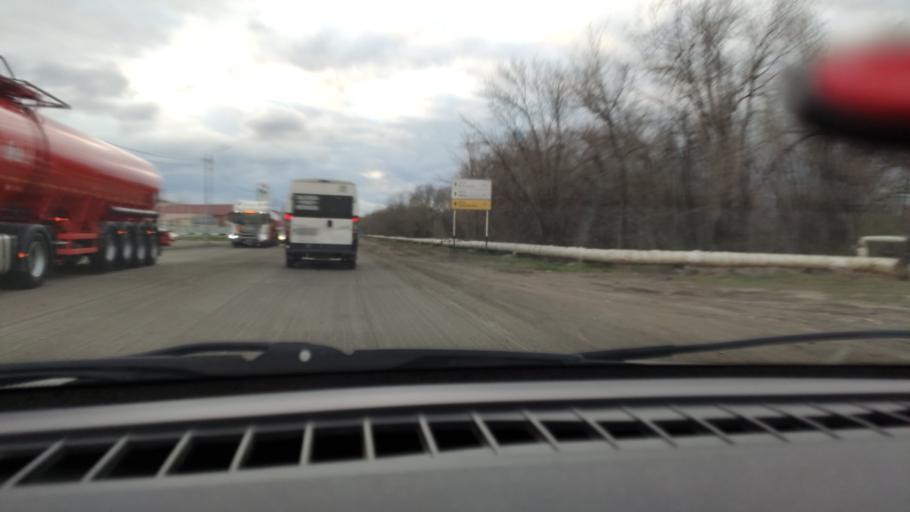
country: RU
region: Orenburg
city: Prigorodnyy
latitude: 51.7825
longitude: 55.1867
